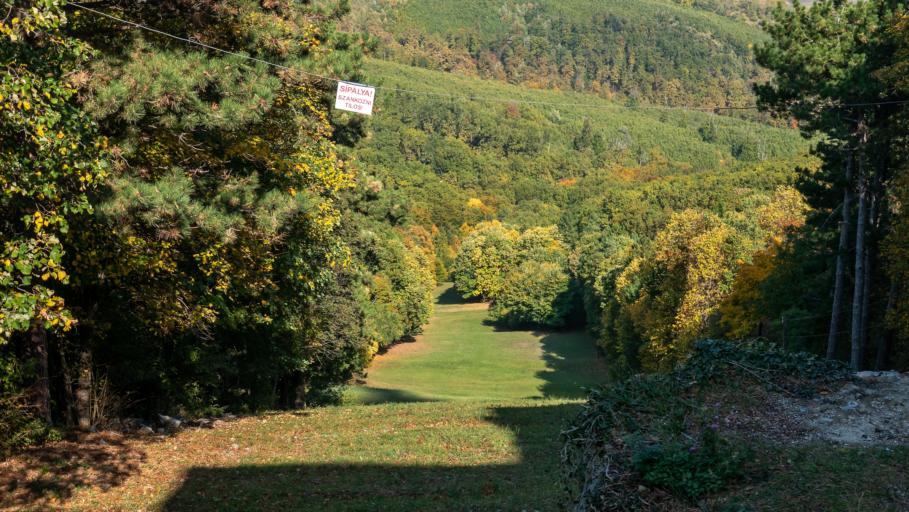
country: HU
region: Baranya
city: Pecs
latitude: 46.1009
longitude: 18.2204
